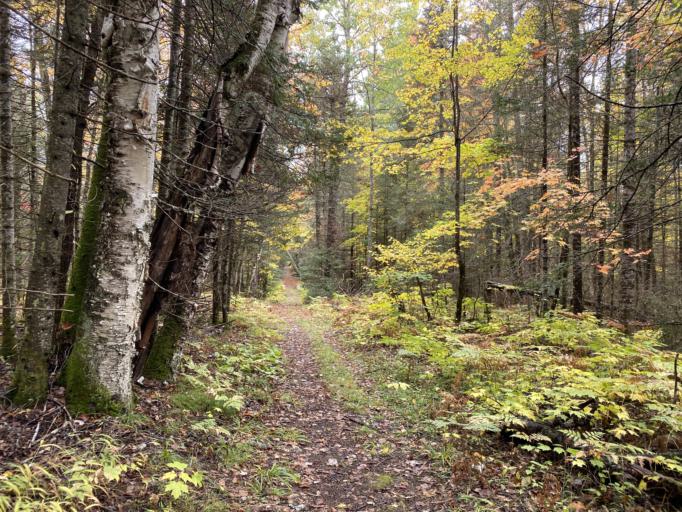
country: US
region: Michigan
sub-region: Marquette County
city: West Ishpeming
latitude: 46.5339
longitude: -87.9990
